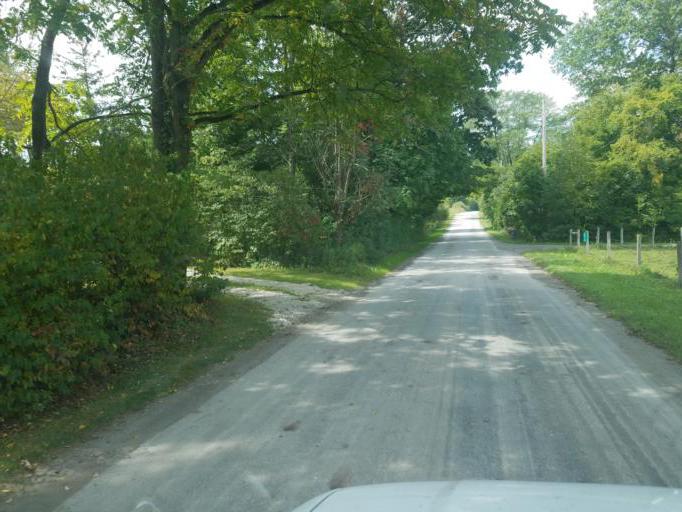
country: US
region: Ohio
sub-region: Geauga County
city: Middlefield
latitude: 41.4258
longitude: -80.9754
